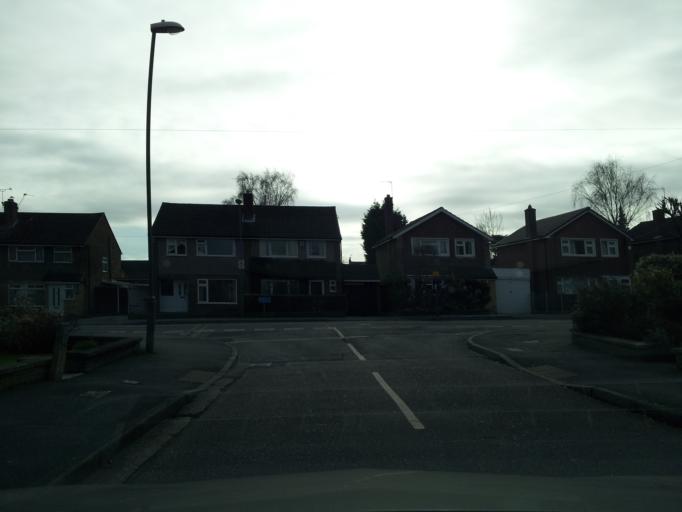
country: GB
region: England
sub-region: Derbyshire
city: Findern
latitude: 52.9170
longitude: -1.5362
